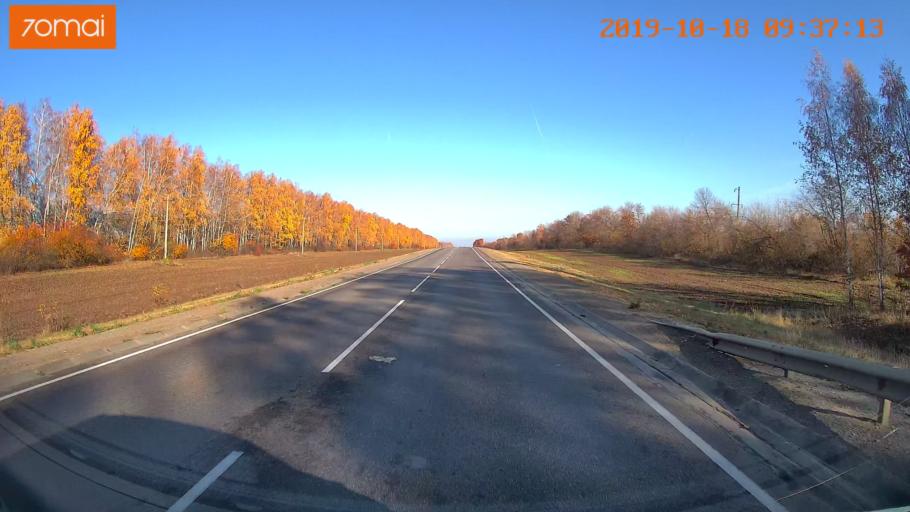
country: RU
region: Tula
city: Yefremov
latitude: 53.2185
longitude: 38.1420
